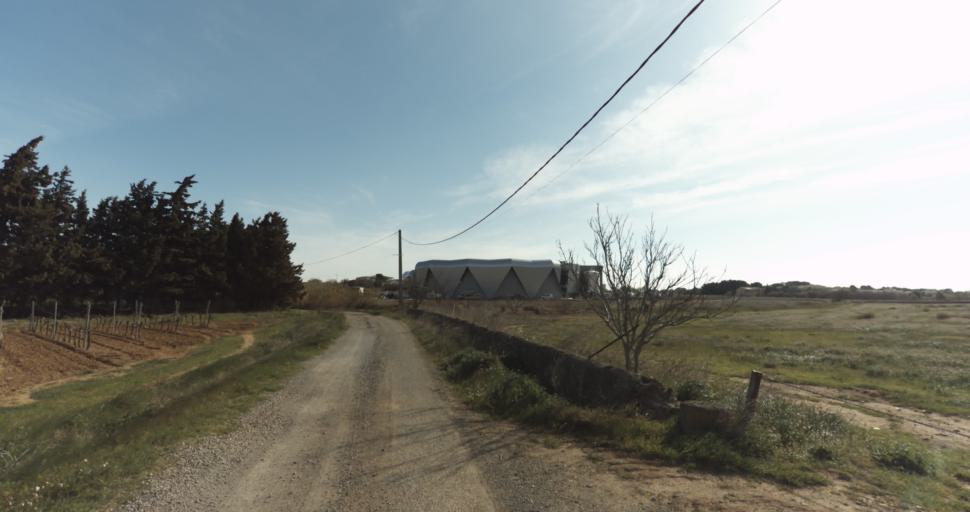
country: FR
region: Languedoc-Roussillon
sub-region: Departement de l'Herault
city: Marseillan
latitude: 43.3559
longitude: 3.5134
